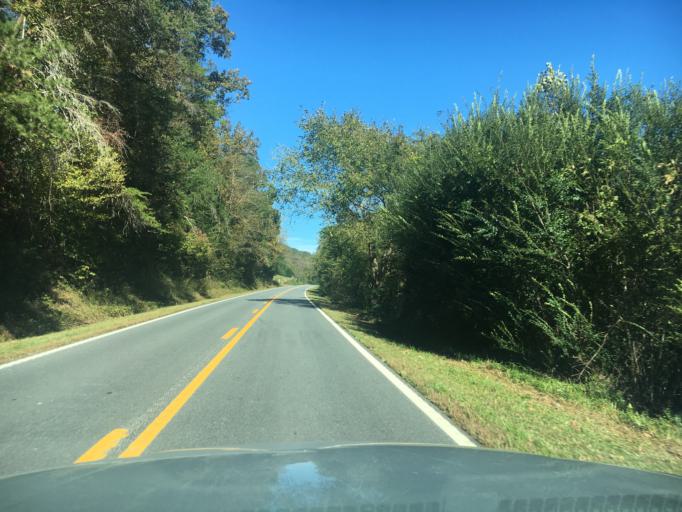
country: US
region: North Carolina
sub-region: Rutherford County
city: Spindale
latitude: 35.5276
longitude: -81.8559
